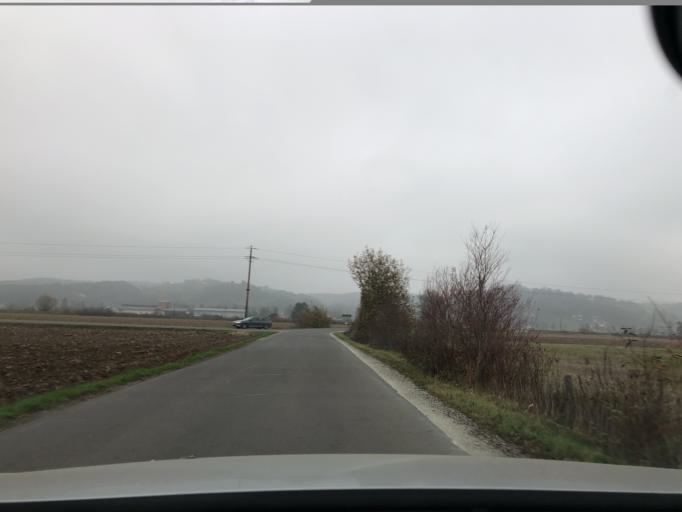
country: AT
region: Styria
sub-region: Politischer Bezirk Suedoststeiermark
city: Fehring
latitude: 46.9453
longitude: 16.0315
